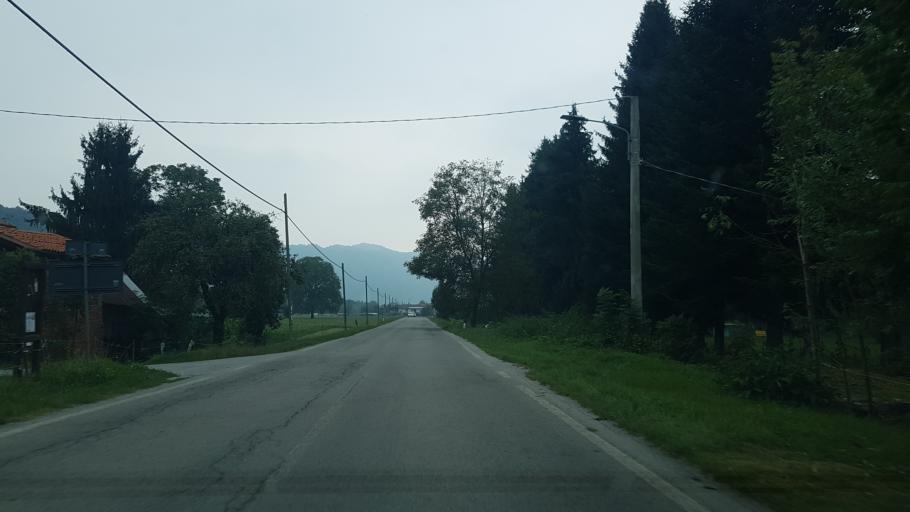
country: IT
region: Piedmont
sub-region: Provincia di Cuneo
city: Roccaforte Mondovi
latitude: 44.2995
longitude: 7.7458
